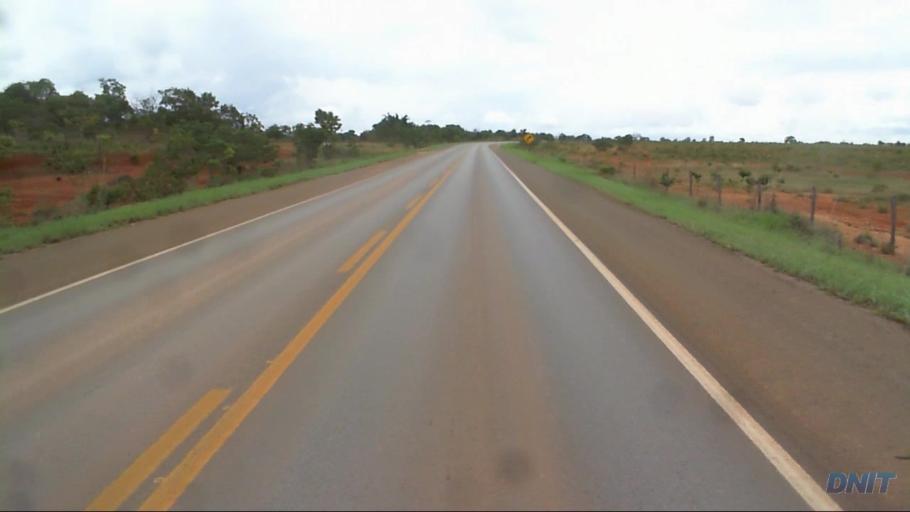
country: BR
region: Goias
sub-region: Padre Bernardo
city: Padre Bernardo
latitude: -15.1530
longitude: -48.3510
